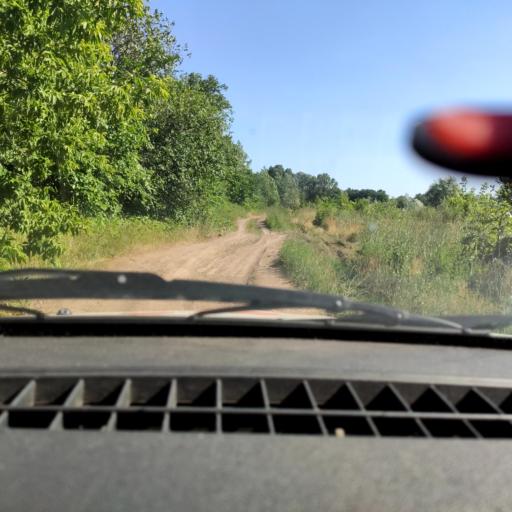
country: RU
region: Bashkortostan
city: Sterlitamak
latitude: 53.7455
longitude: 56.0812
